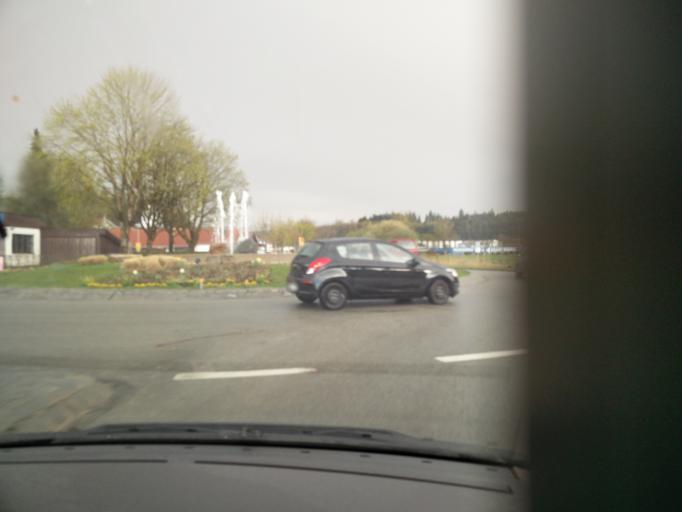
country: DE
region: Bavaria
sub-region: Upper Bavaria
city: Bad Endorf
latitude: 47.9172
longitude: 12.2927
